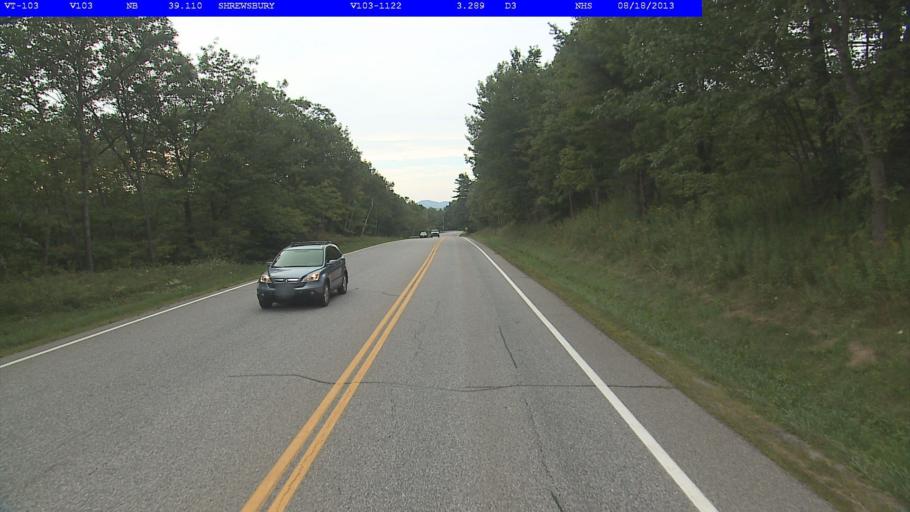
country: US
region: Vermont
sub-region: Rutland County
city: Rutland
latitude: 43.5151
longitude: -72.9173
